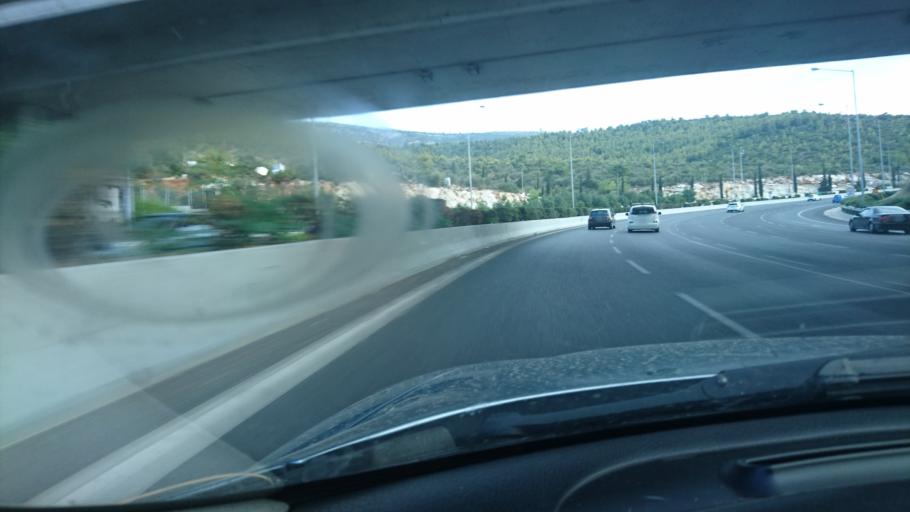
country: GR
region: Attica
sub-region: Nomos Attikis
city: Zografos
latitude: 37.9738
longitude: 23.7932
